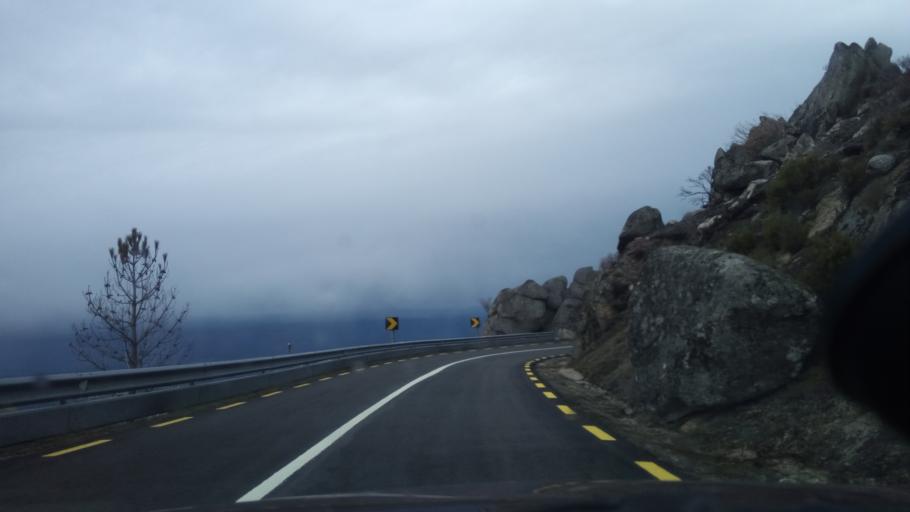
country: PT
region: Guarda
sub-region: Manteigas
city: Manteigas
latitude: 40.4352
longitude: -7.6044
